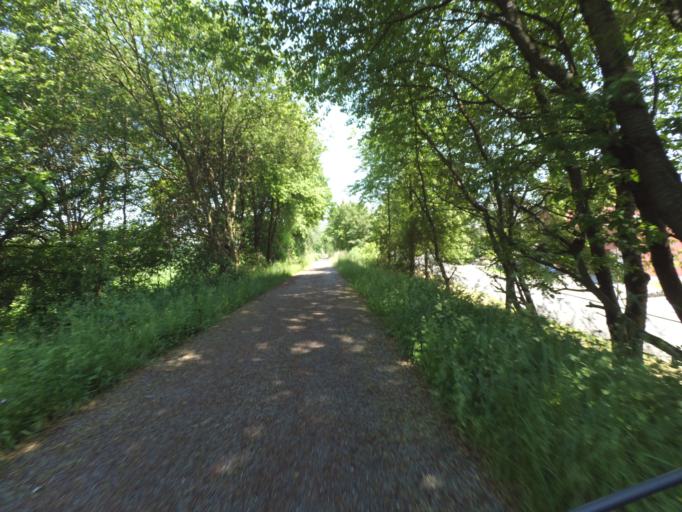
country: DE
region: Rheinland-Pfalz
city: Leiningen
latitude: 50.1337
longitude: 7.5689
